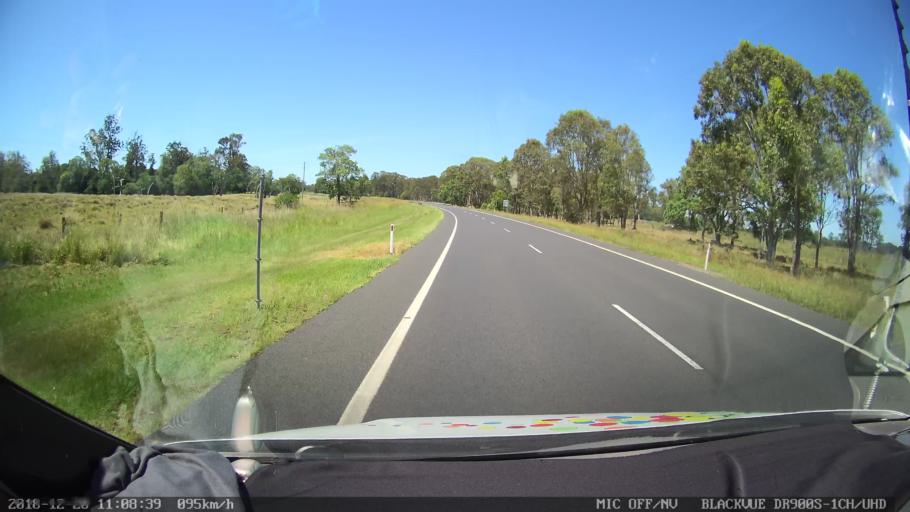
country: AU
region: New South Wales
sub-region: Richmond Valley
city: Casino
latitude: -28.9250
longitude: 153.0051
